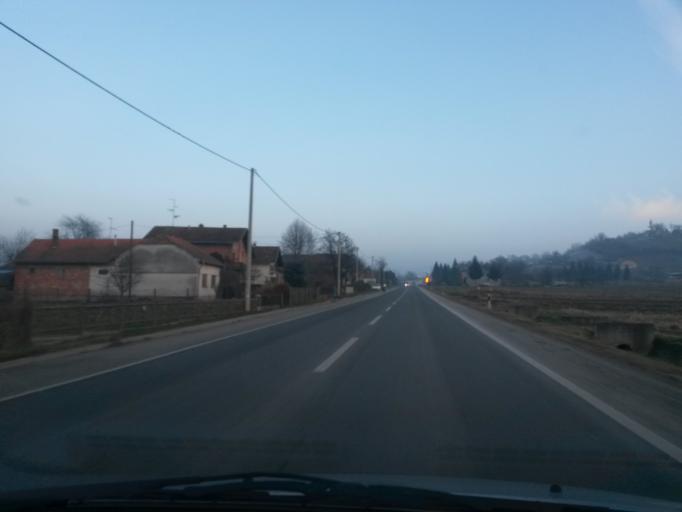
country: HR
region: Varazdinska
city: Ludbreg
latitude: 46.2390
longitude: 16.6354
